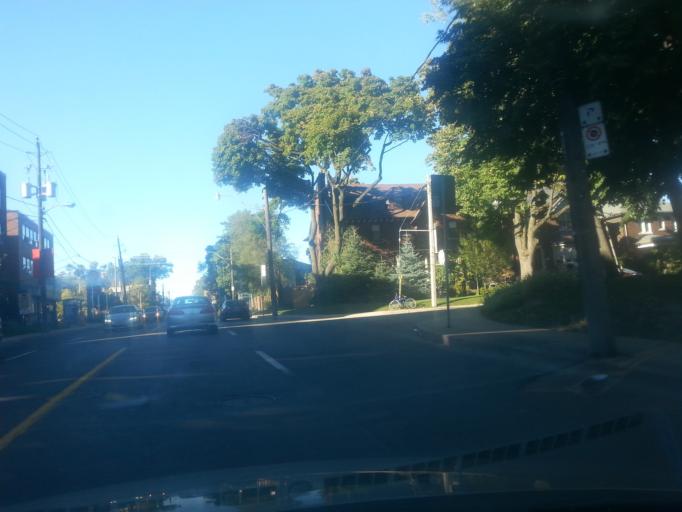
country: CA
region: Ontario
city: Toronto
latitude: 43.6861
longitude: -79.4196
